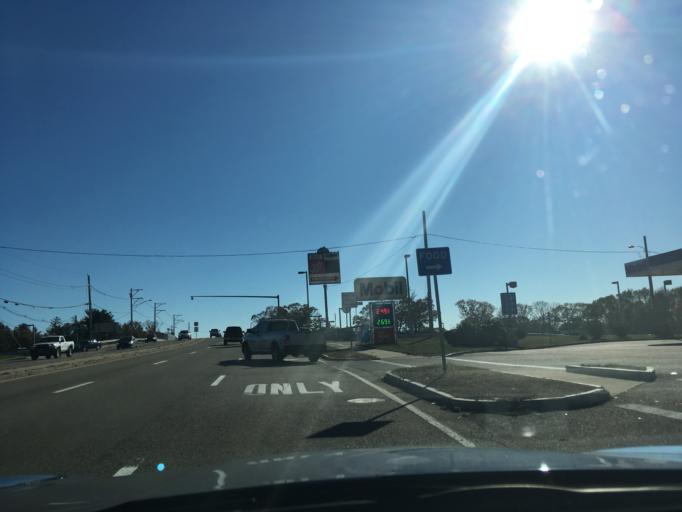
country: US
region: Massachusetts
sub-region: Bristol County
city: North Seekonk
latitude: 41.8996
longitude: -71.3554
